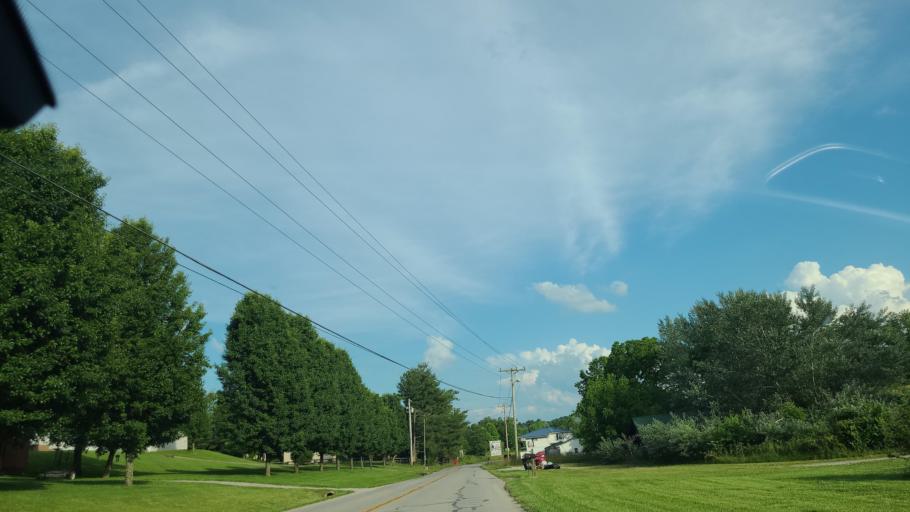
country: US
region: Kentucky
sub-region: Whitley County
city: Corbin
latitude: 36.9040
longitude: -84.2380
